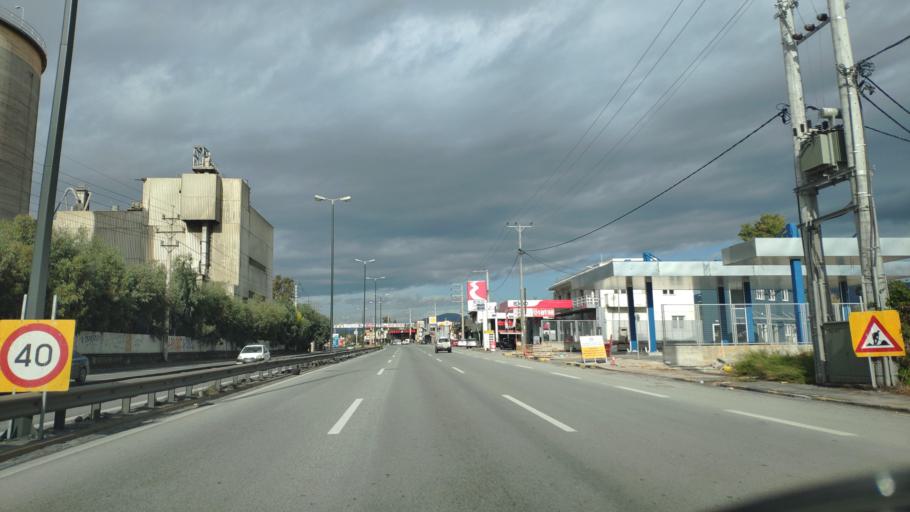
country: GR
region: Attica
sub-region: Nomarchia Dytikis Attikis
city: Aspropyrgos
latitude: 38.0350
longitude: 23.5942
